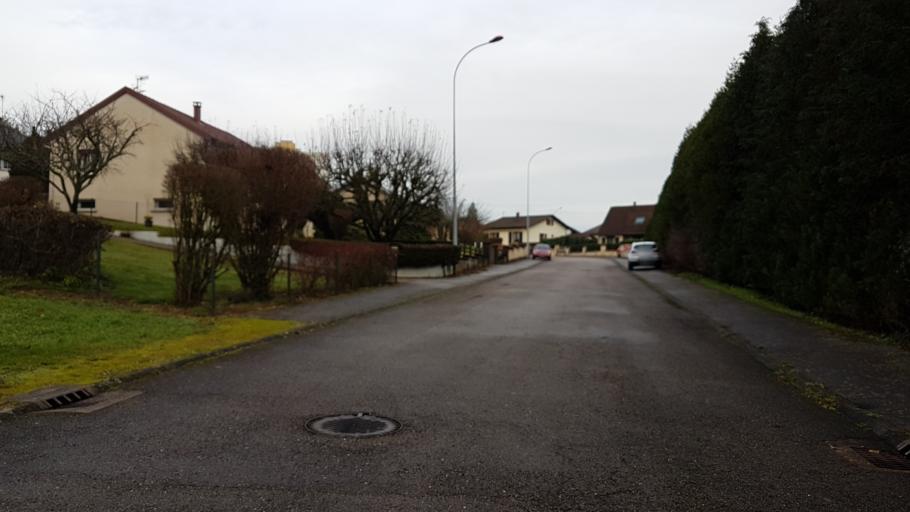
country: FR
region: Franche-Comte
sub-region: Departement de la Haute-Saone
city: Luxeuil-les-Bains
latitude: 47.8117
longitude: 6.3723
